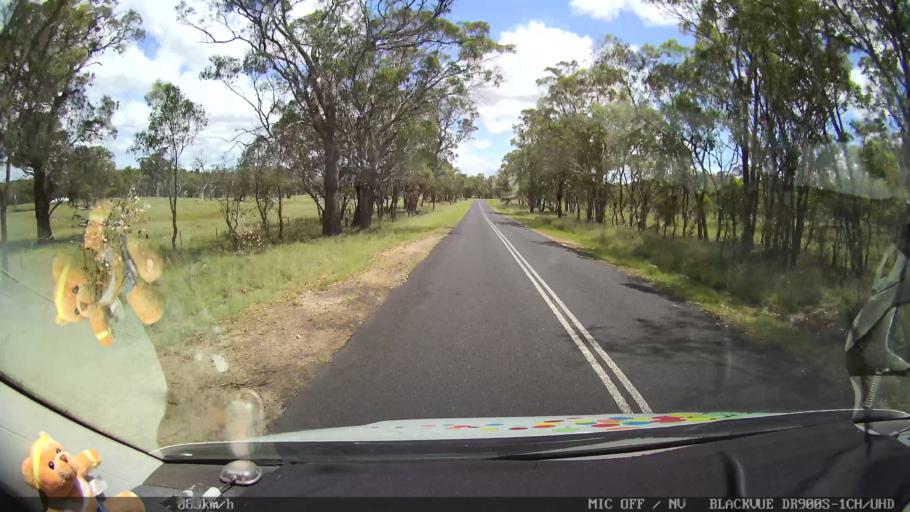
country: AU
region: New South Wales
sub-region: Glen Innes Severn
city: Glen Innes
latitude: -29.5253
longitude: 151.6741
